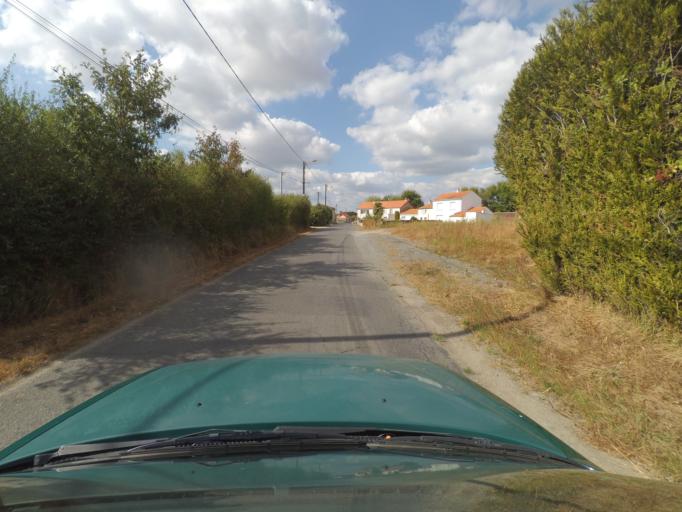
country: FR
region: Pays de la Loire
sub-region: Departement de la Loire-Atlantique
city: Aigrefeuille-sur-Maine
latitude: 47.0662
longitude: -1.3990
